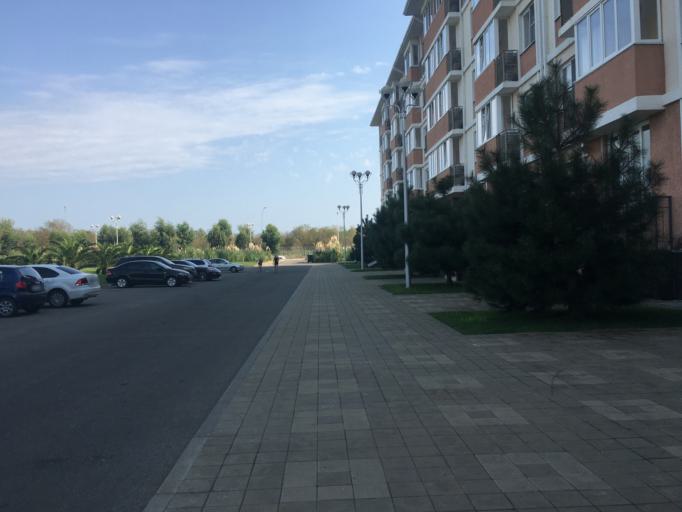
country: RU
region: Krasnodarskiy
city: Vysokoye
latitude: 43.3899
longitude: 39.9959
